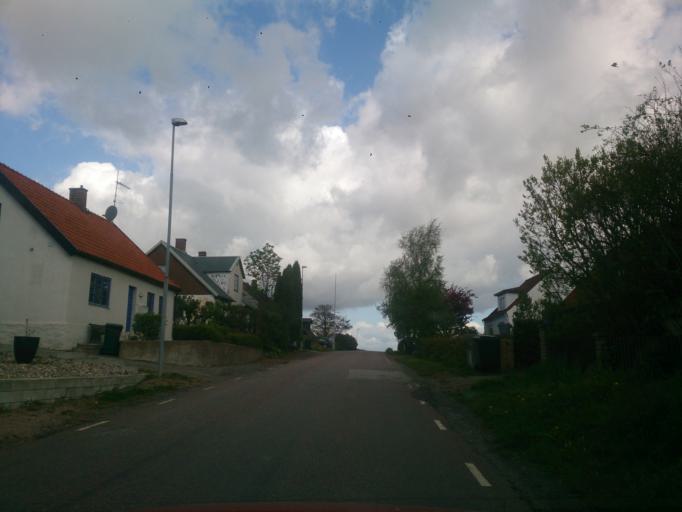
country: SE
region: Skane
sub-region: Ystads Kommun
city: Ystad
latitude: 55.4476
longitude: 13.7161
